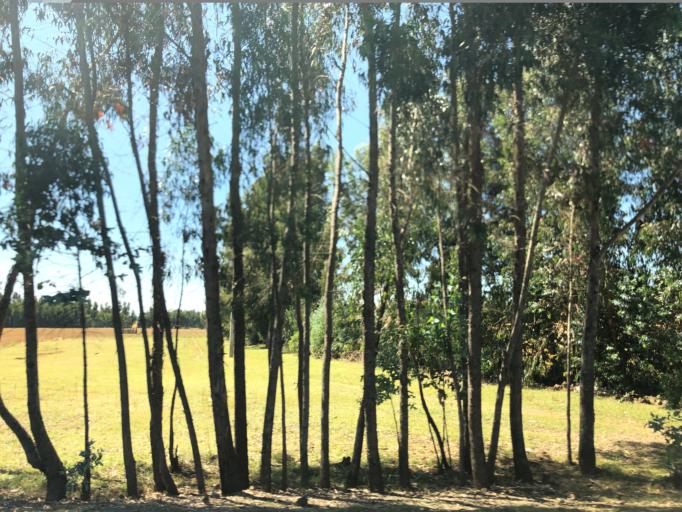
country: ET
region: Amhara
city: Lalibela
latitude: 11.7274
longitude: 38.7612
